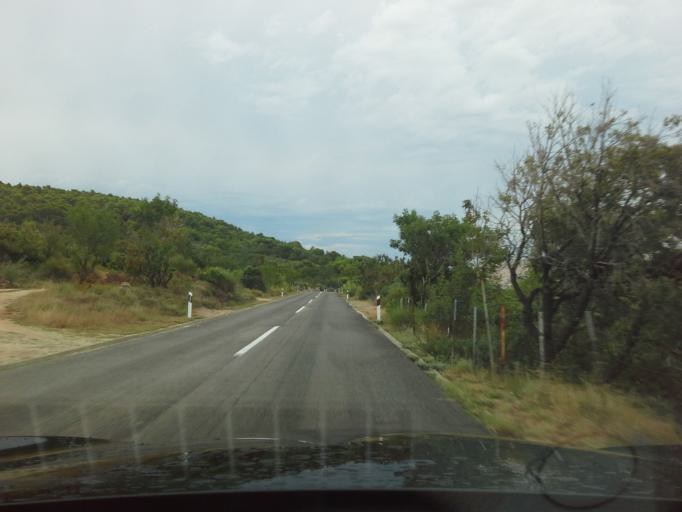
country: HR
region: Primorsko-Goranska
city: Banjol
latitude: 44.7204
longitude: 14.8234
